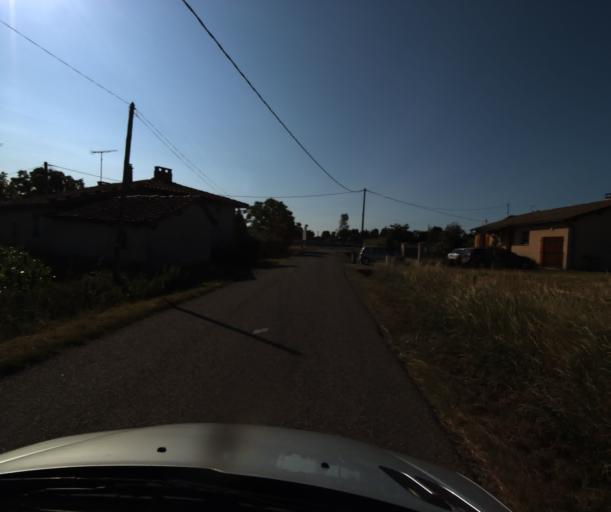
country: FR
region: Midi-Pyrenees
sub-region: Departement du Tarn-et-Garonne
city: Bressols
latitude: 43.9689
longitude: 1.3301
